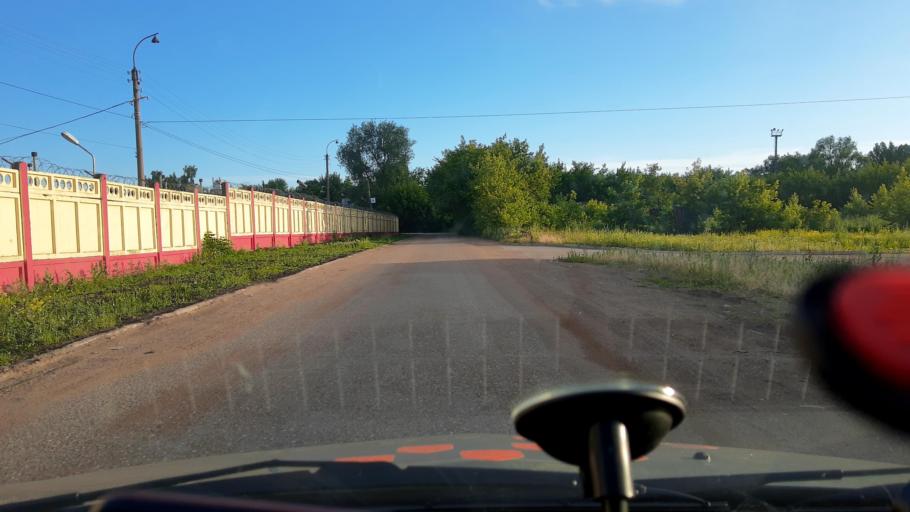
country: RU
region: Bashkortostan
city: Ufa
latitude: 54.7973
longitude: 56.0992
